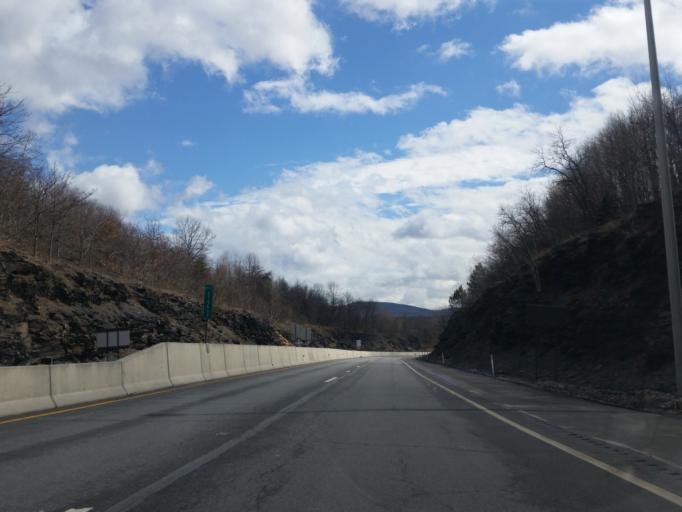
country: US
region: Pennsylvania
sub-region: Lackawanna County
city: Old Forge
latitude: 41.3815
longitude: -75.7245
